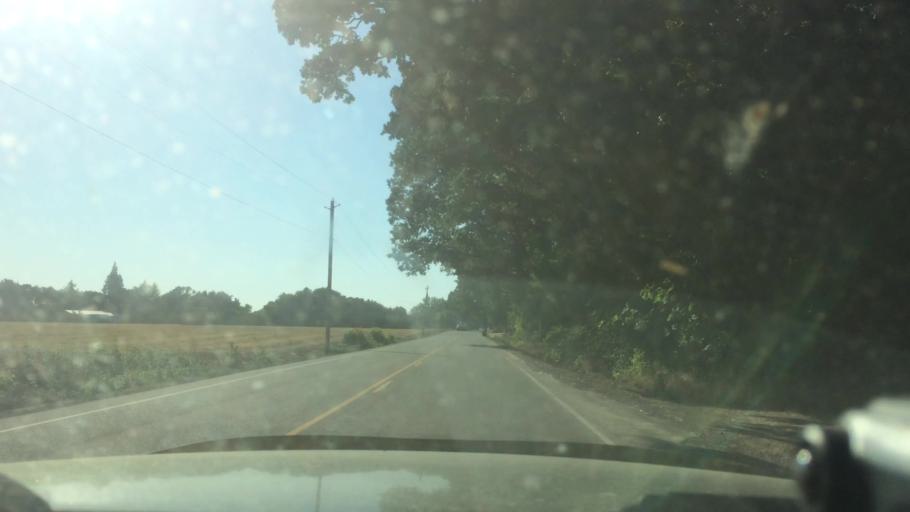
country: US
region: Oregon
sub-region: Marion County
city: Gervais
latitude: 45.1278
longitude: -122.9952
